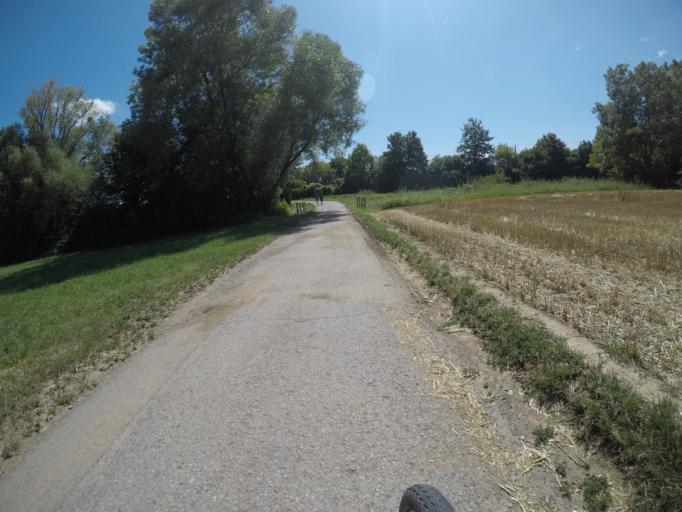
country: DE
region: Baden-Wuerttemberg
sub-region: Regierungsbezirk Stuttgart
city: Leinfelden-Echterdingen
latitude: 48.7254
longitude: 9.1343
